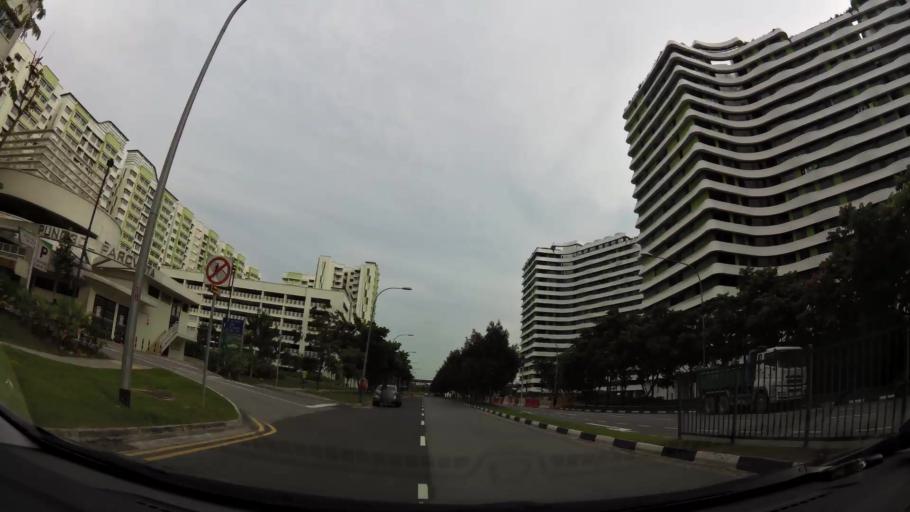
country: MY
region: Johor
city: Kampung Pasir Gudang Baru
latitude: 1.4104
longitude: 103.9004
